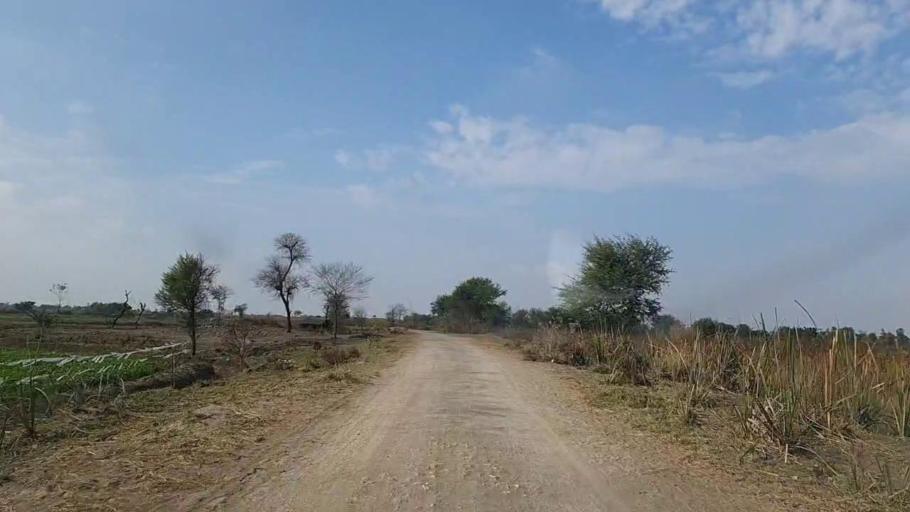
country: PK
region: Sindh
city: Sanghar
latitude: 26.2543
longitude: 69.0107
